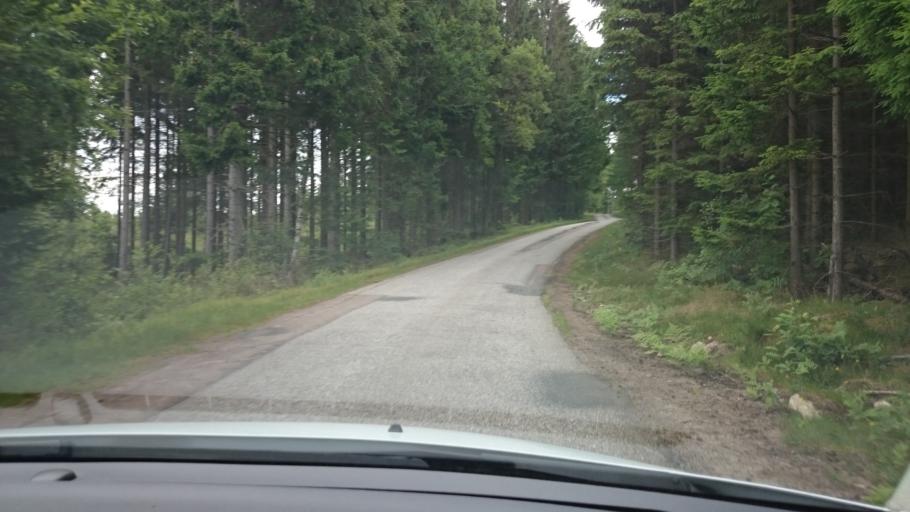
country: SE
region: Halland
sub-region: Hylte Kommun
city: Hyltebruk
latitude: 56.9620
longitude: 13.1851
